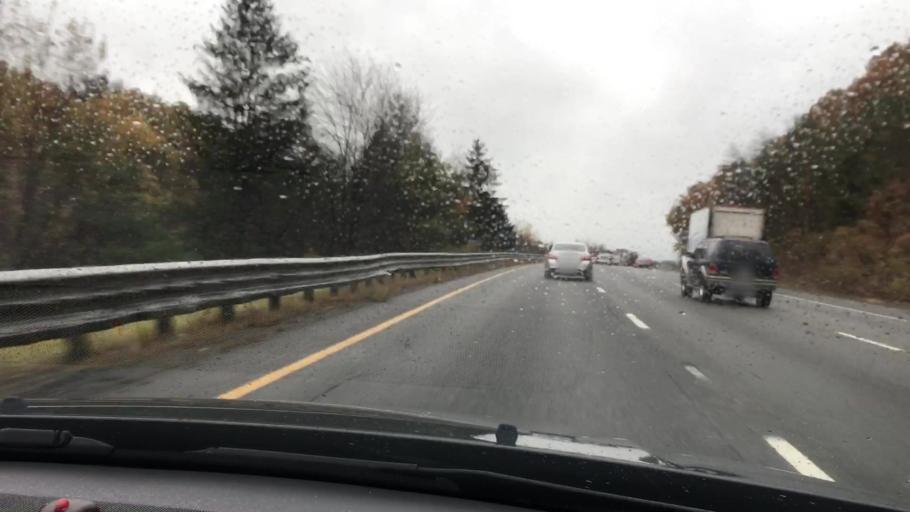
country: US
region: Massachusetts
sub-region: Middlesex County
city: Westford
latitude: 42.5590
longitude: -71.4404
